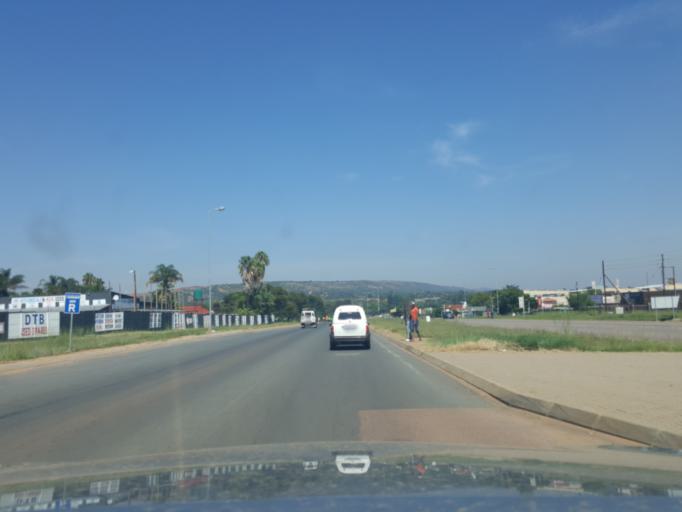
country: ZA
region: Gauteng
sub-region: City of Tshwane Metropolitan Municipality
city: Pretoria
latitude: -25.6843
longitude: 28.2990
